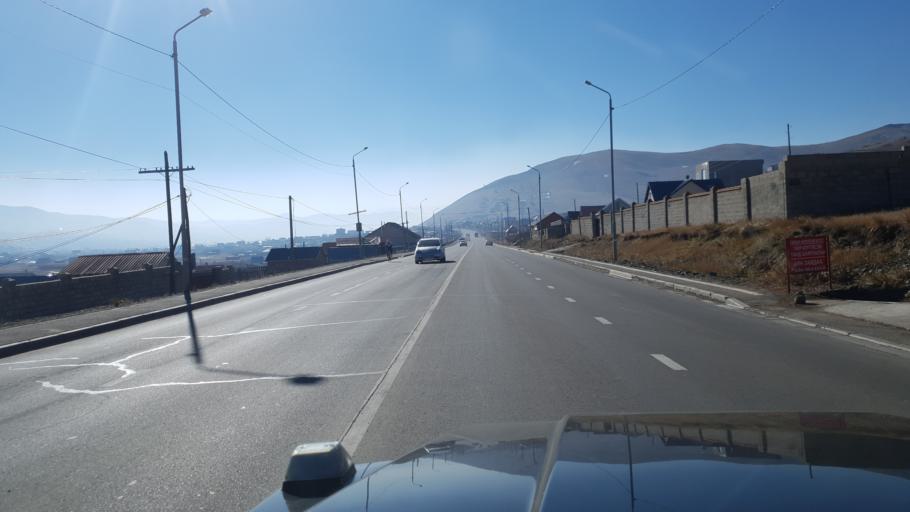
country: MN
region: Ulaanbaatar
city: Ulaanbaatar
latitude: 48.0234
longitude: 106.9141
